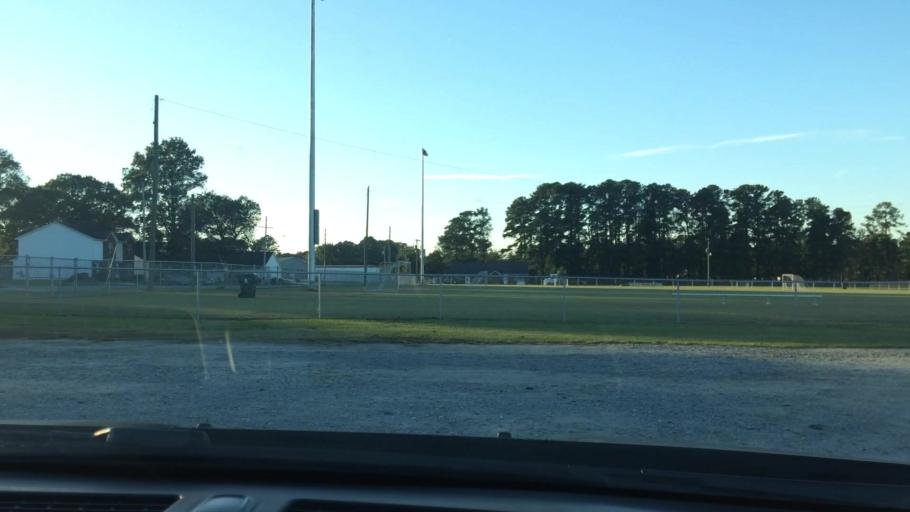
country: US
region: North Carolina
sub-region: Pitt County
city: Farmville
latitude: 35.6012
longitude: -77.5862
